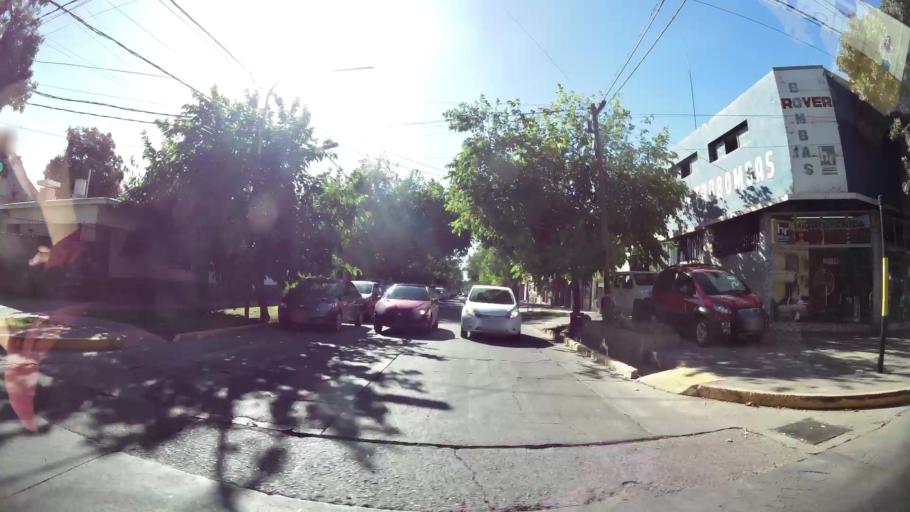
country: AR
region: Mendoza
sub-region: Departamento de Godoy Cruz
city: Godoy Cruz
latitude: -32.9150
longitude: -68.8425
